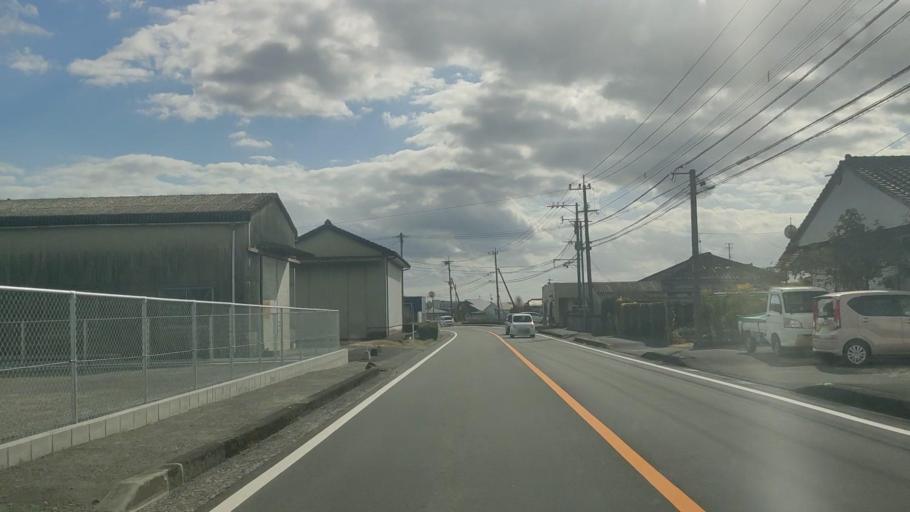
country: JP
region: Kagoshima
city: Kajiki
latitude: 31.8071
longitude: 130.7091
